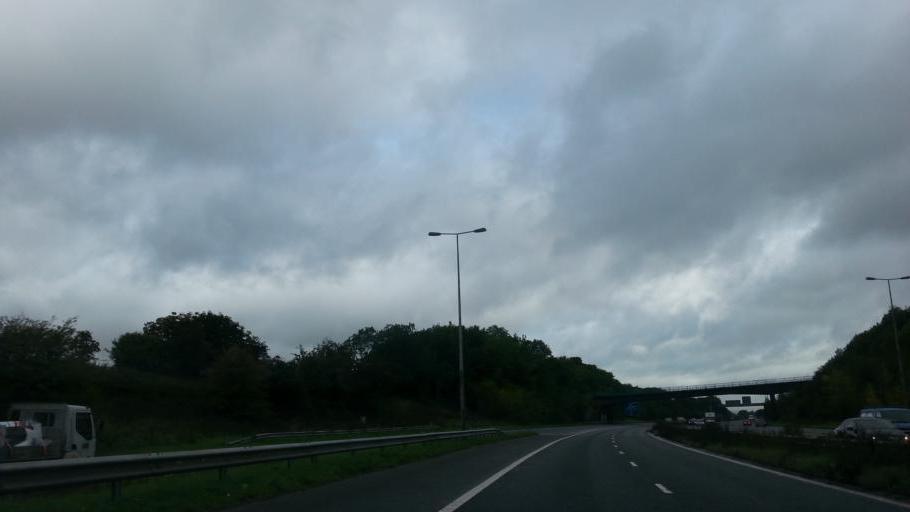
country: GB
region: England
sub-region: Borough of Oldham
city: Royton
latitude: 53.5763
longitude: -2.1607
